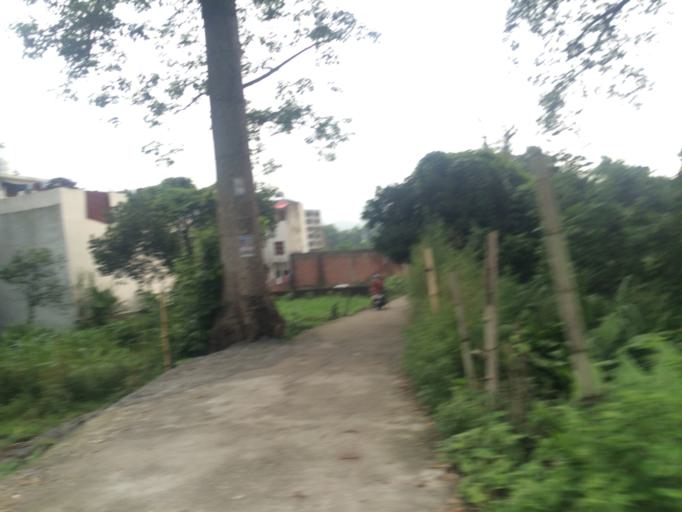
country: IN
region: Uttarakhand
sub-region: Dehradun
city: Birbhaddar
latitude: 30.0739
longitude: 78.2787
